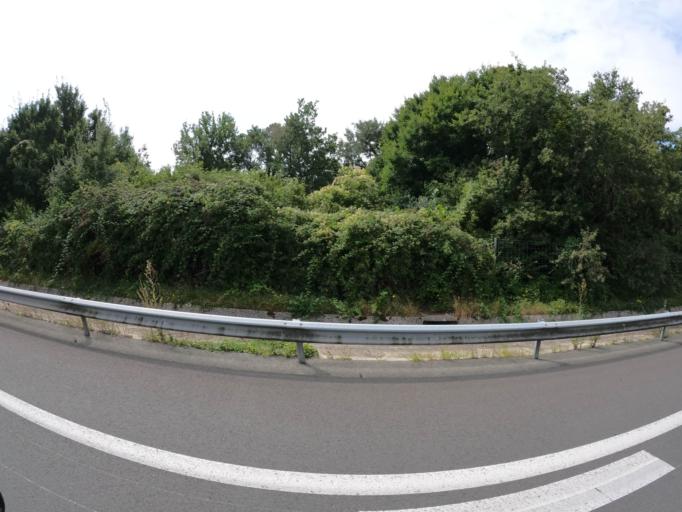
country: FR
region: Poitou-Charentes
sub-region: Departement de la Charente-Maritime
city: Courcon
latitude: 46.2218
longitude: -0.8141
